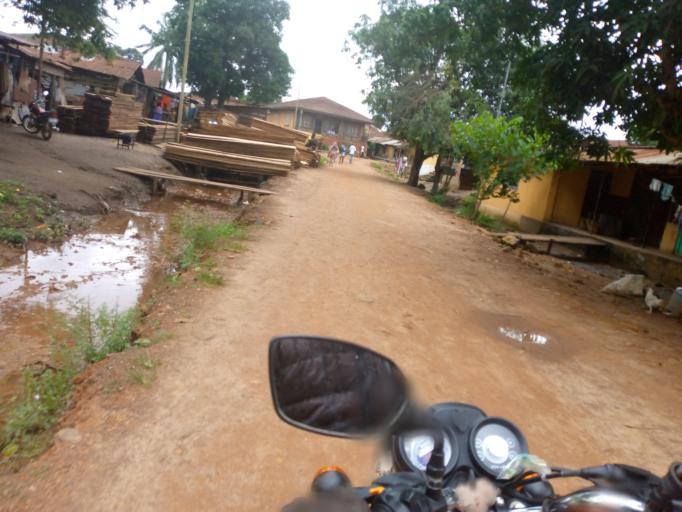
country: SL
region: Eastern Province
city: Kenema
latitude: 7.8787
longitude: -11.1862
